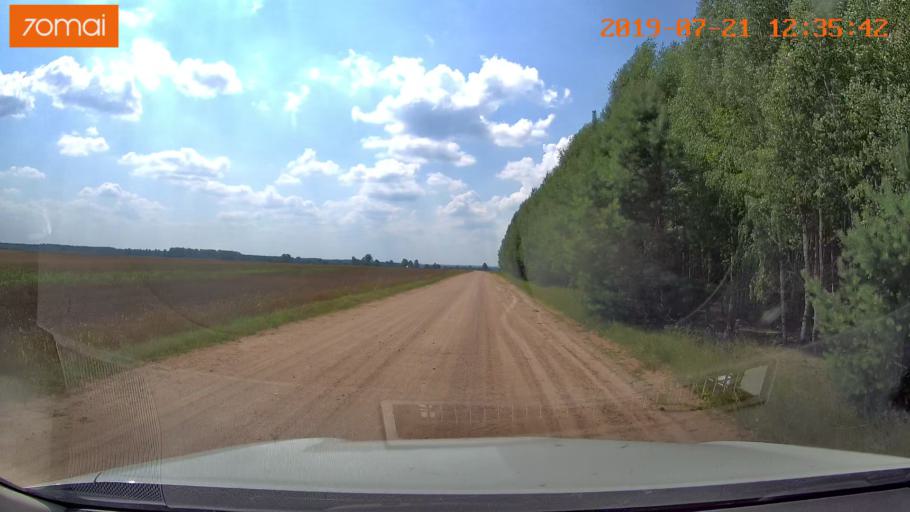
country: BY
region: Grodnenskaya
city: Lyubcha
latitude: 53.8748
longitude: 26.0058
